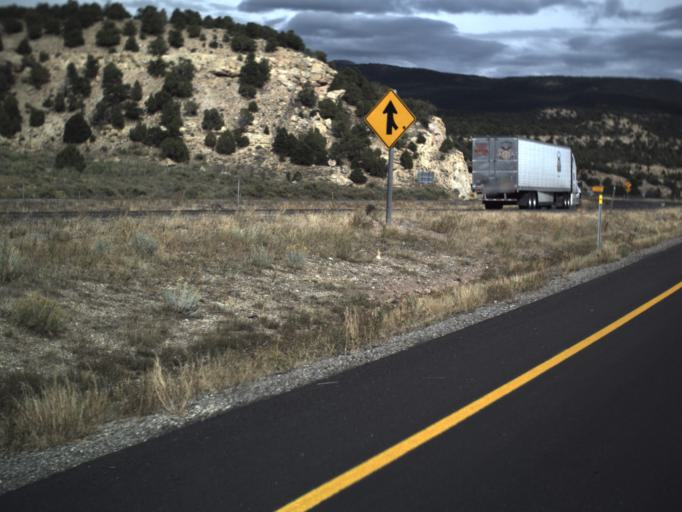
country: US
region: Utah
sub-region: Sevier County
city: Salina
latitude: 38.9155
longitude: -111.7364
